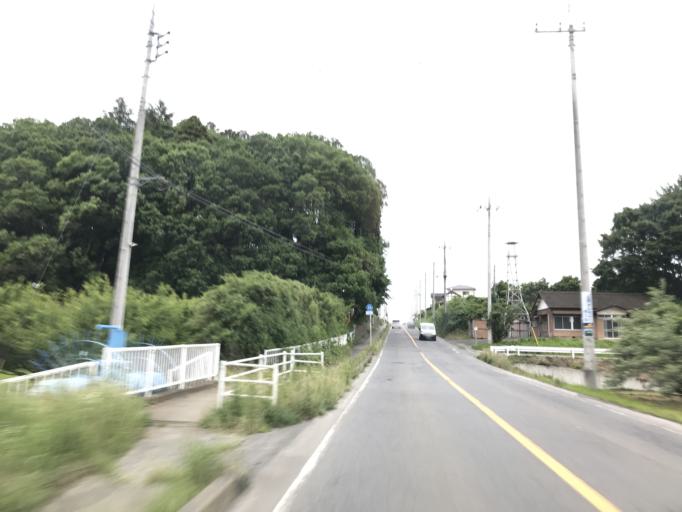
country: JP
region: Ibaraki
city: Ishioka
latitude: 36.2212
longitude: 140.3013
